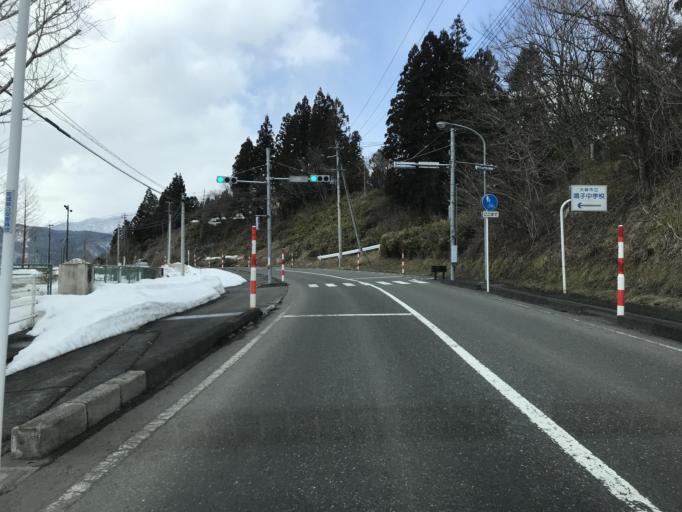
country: JP
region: Miyagi
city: Furukawa
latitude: 38.7372
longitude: 140.7660
